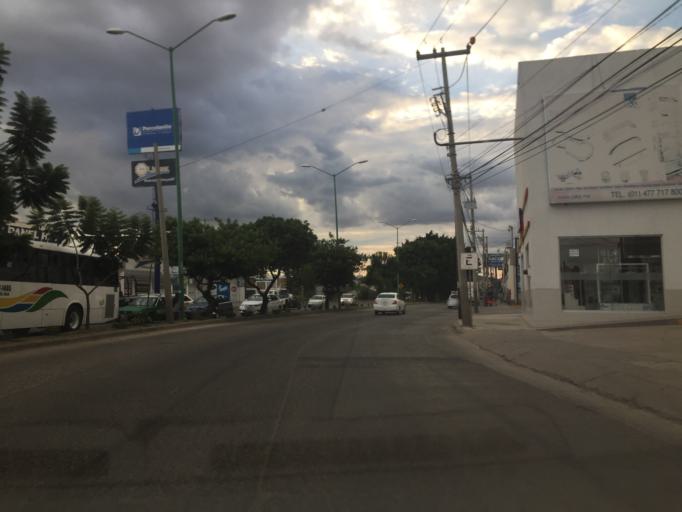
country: MX
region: Guanajuato
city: Leon
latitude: 21.1467
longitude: -101.6724
